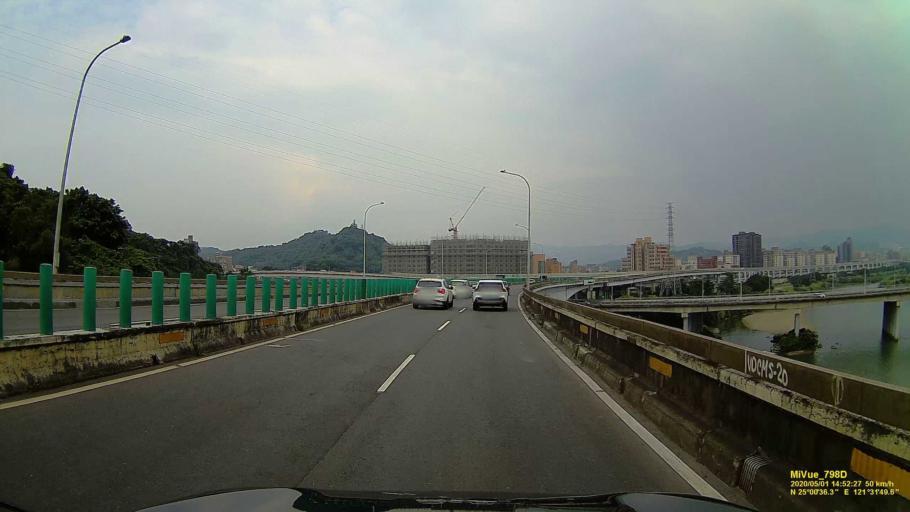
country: TW
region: Taipei
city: Taipei
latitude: 25.0102
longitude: 121.5311
